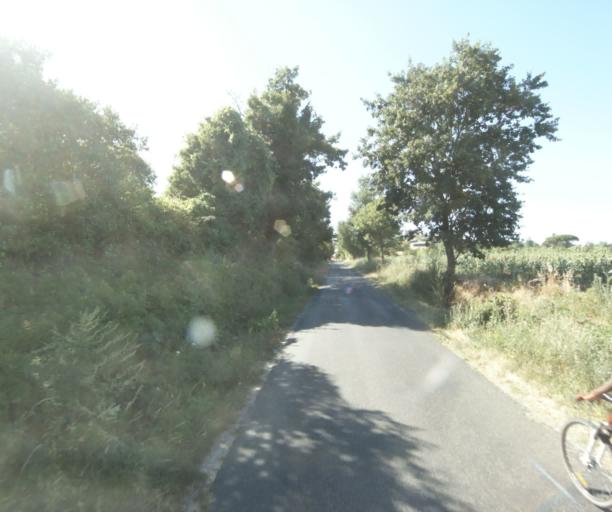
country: FR
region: Midi-Pyrenees
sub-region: Departement de la Haute-Garonne
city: Revel
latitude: 43.5040
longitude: 1.9430
